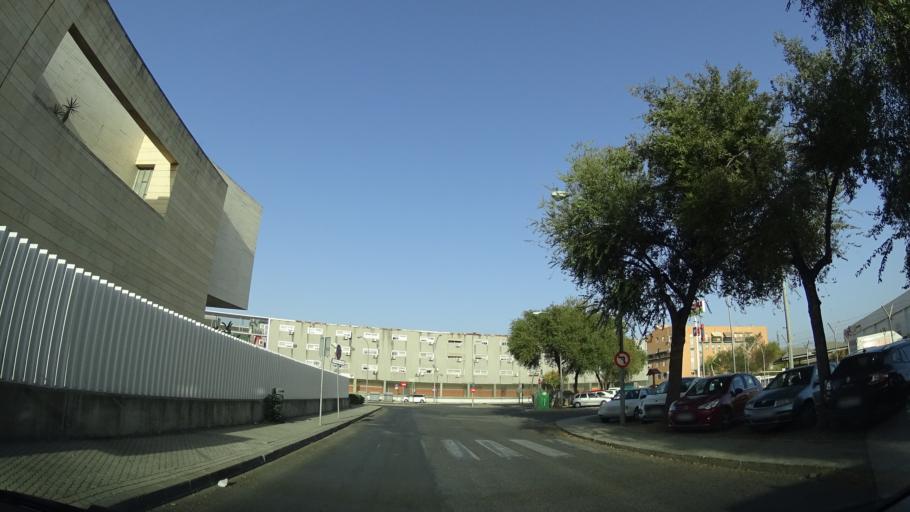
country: ES
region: Andalusia
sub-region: Provincia de Sevilla
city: La Algaba
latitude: 37.4316
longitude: -5.9793
